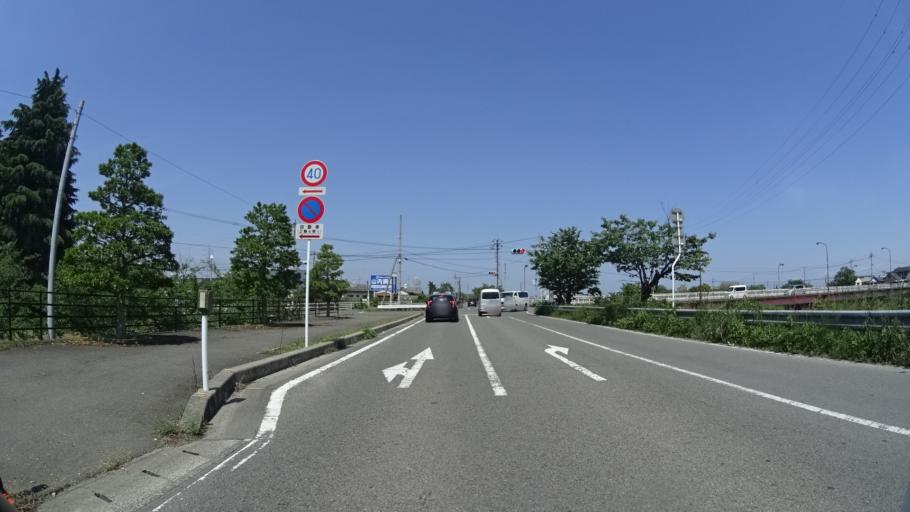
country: JP
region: Ehime
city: Hojo
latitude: 34.0496
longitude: 132.9885
